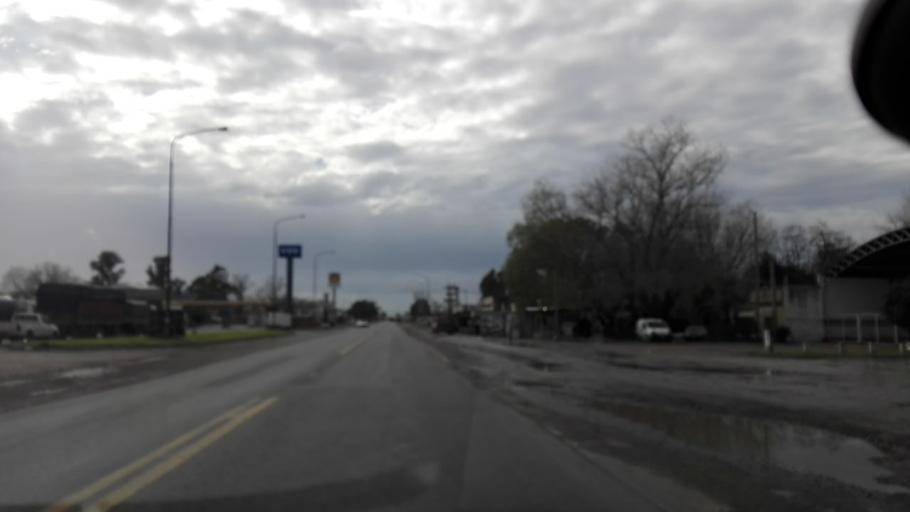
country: AR
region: Buenos Aires
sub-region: Partido de Las Flores
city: Las Flores
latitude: -36.0287
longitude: -59.0849
